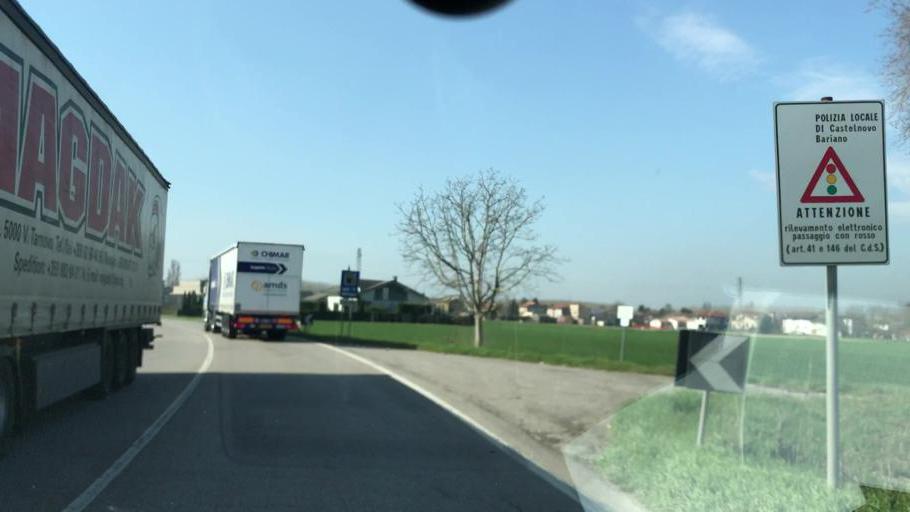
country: IT
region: Veneto
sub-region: Provincia di Rovigo
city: Castelnovo Bariano
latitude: 45.0275
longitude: 11.2968
